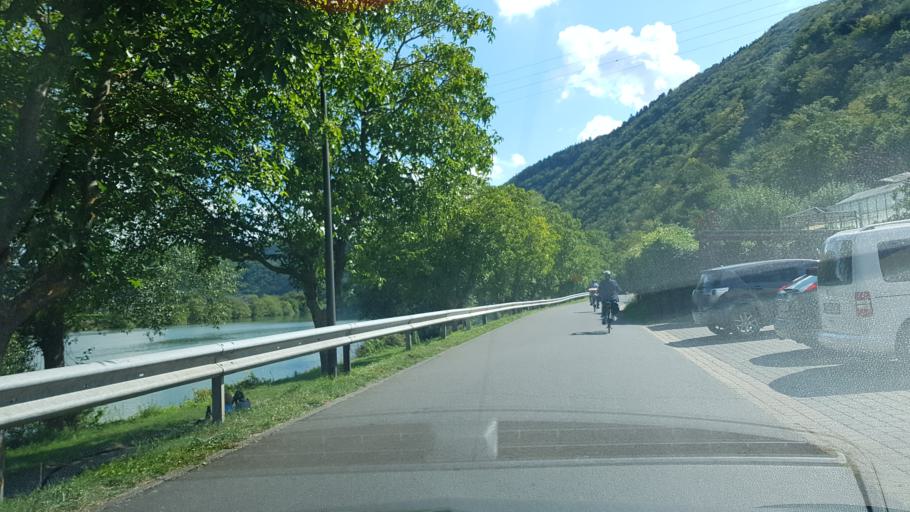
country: DE
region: Rheinland-Pfalz
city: Mesenich
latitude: 50.1079
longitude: 7.2141
